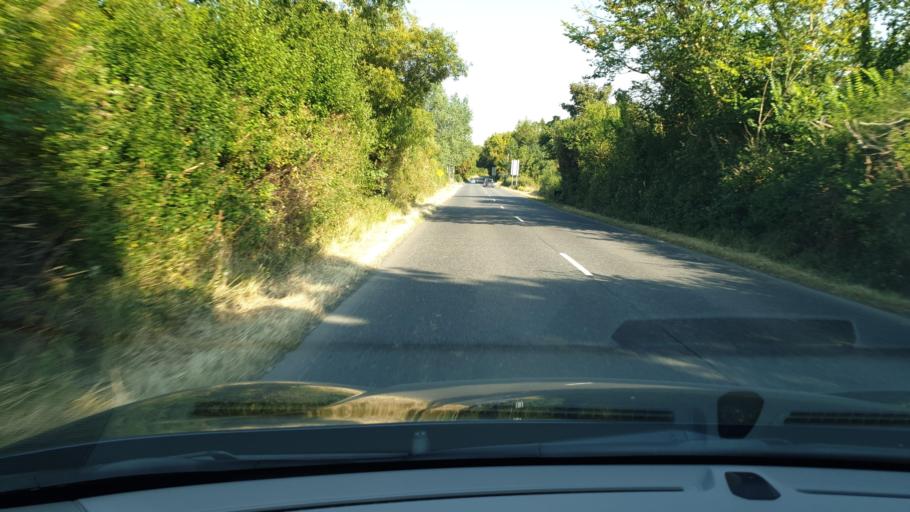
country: IE
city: Kentstown
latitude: 53.6262
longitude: -6.5269
